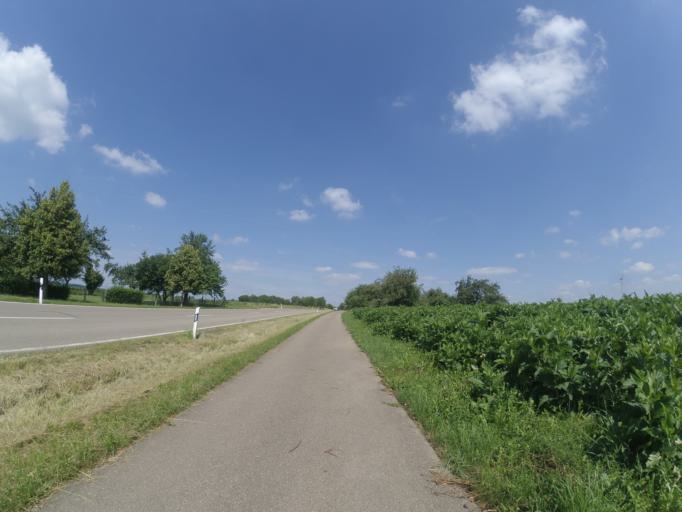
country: DE
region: Baden-Wuerttemberg
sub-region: Tuebingen Region
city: Blaubeuren
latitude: 48.4566
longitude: 9.8559
